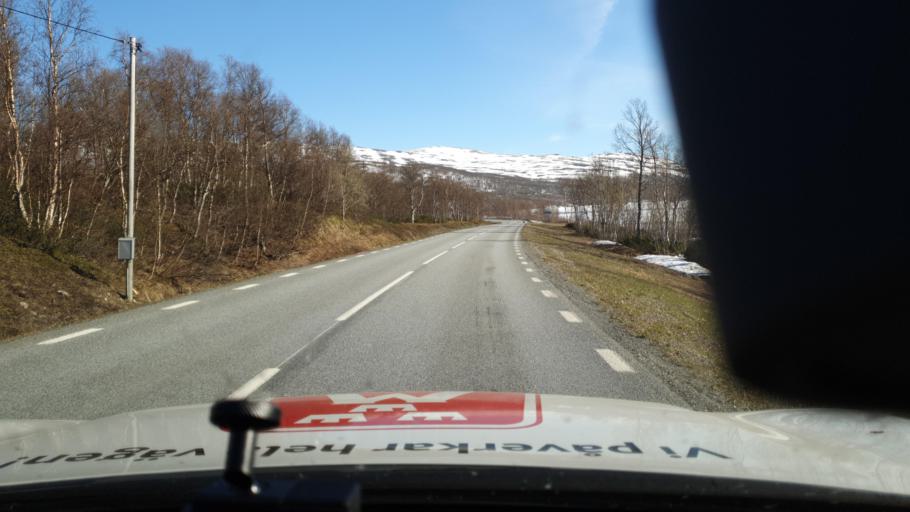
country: NO
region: Nordland
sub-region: Rana
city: Mo i Rana
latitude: 66.0180
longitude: 15.0903
